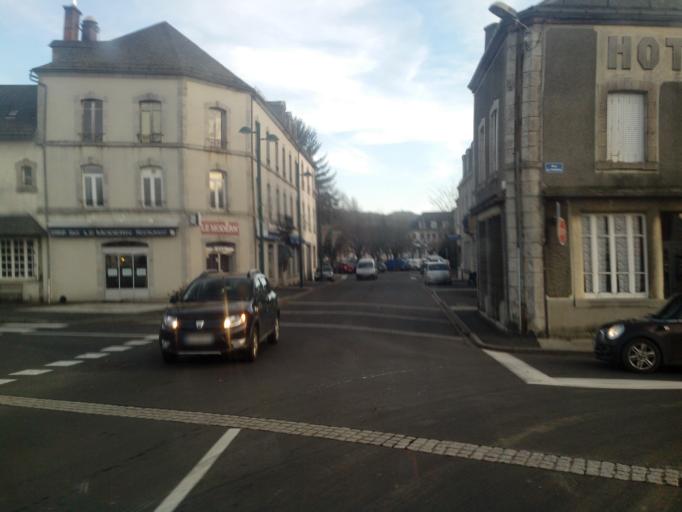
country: FR
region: Auvergne
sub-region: Departement du Cantal
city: Riom-es-Montagnes
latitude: 45.2846
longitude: 2.6583
